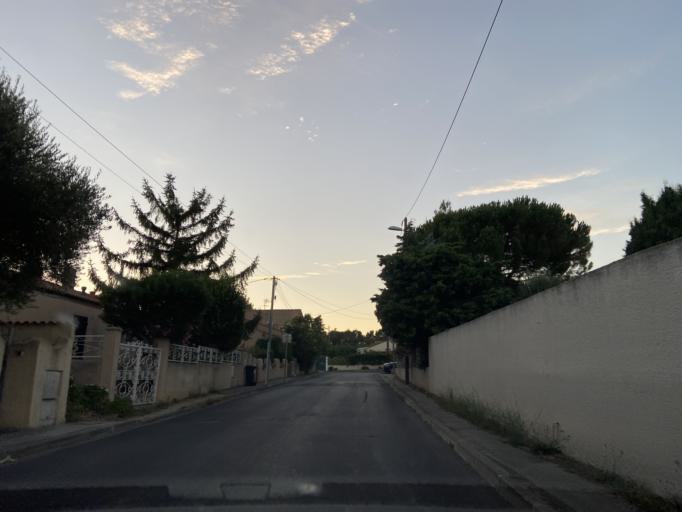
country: FR
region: Provence-Alpes-Cote d'Azur
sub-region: Departement des Bouches-du-Rhone
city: Plan-de-Cuques
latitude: 43.3270
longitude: 5.4480
